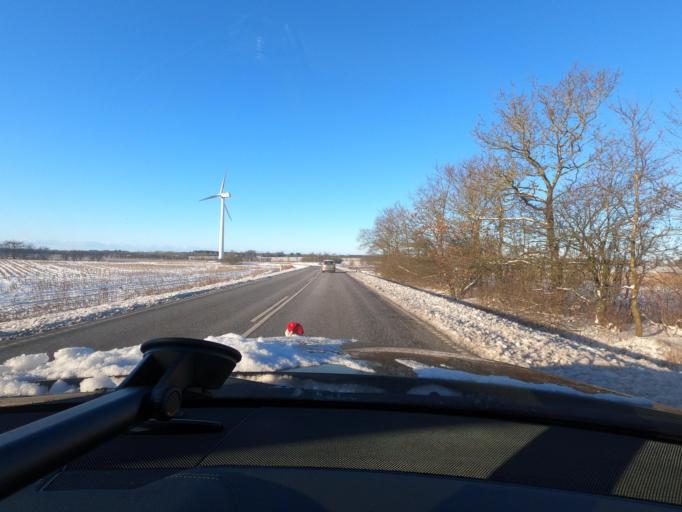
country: DK
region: South Denmark
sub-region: Tonder Kommune
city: Toftlund
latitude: 55.1082
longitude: 9.1797
